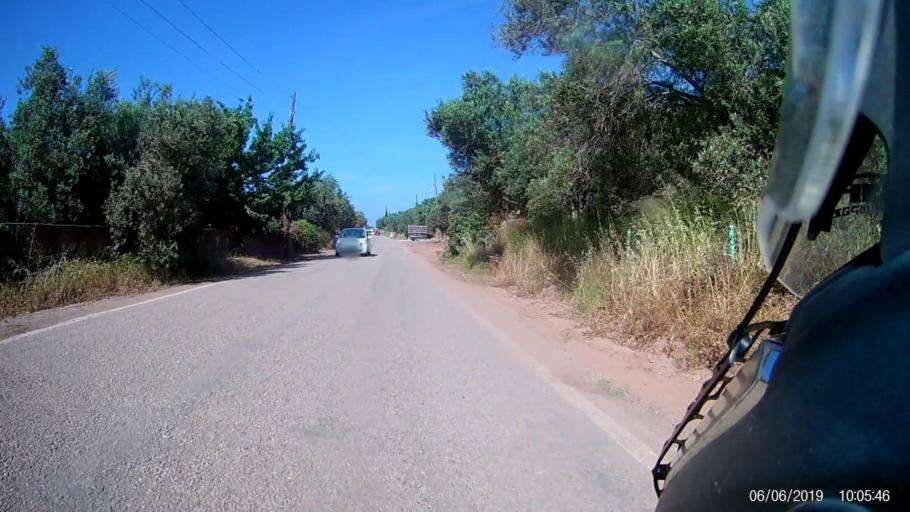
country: TR
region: Canakkale
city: Ayvacik
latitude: 39.5258
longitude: 26.4767
